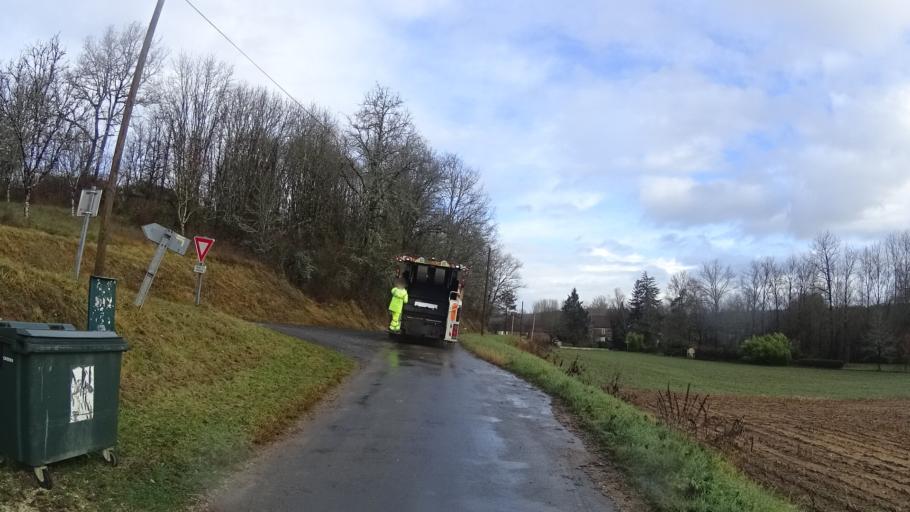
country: FR
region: Aquitaine
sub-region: Departement de la Dordogne
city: Thiviers
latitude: 45.3440
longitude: 0.9487
